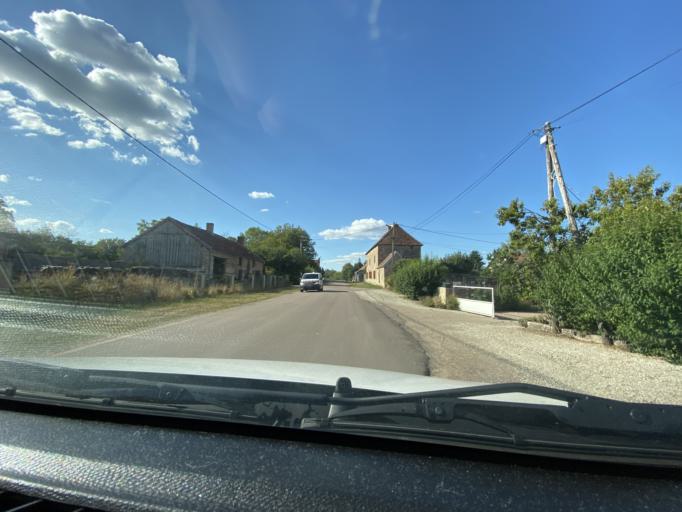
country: FR
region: Bourgogne
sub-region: Departement de la Cote-d'Or
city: Saulieu
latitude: 47.3151
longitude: 4.2012
